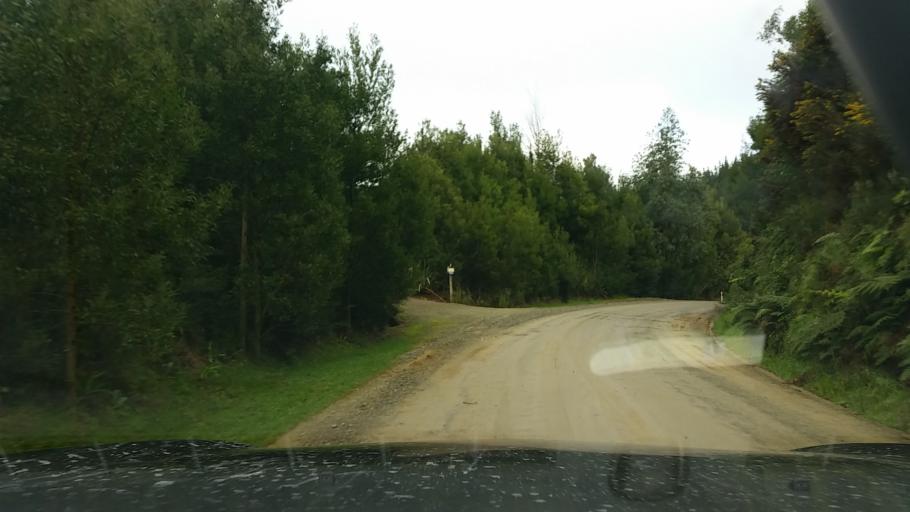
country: NZ
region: Marlborough
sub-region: Marlborough District
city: Picton
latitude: -41.1771
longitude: 174.0734
